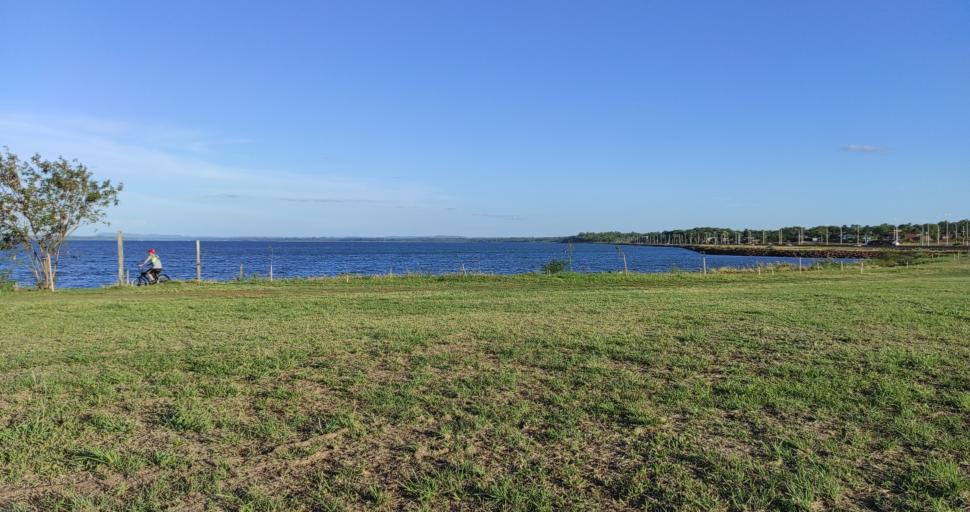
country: AR
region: Misiones
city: Garupa
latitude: -27.4320
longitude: -55.8628
